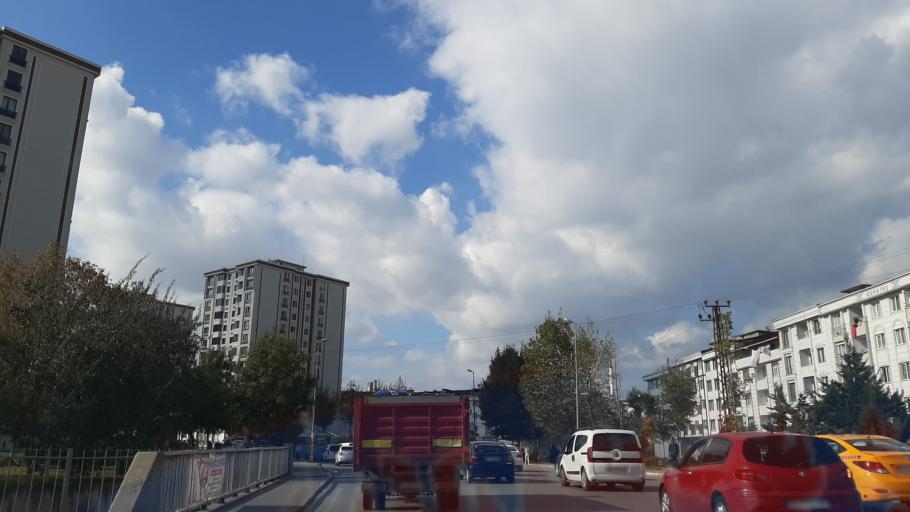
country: TR
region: Istanbul
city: Esenyurt
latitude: 41.0295
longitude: 28.6659
